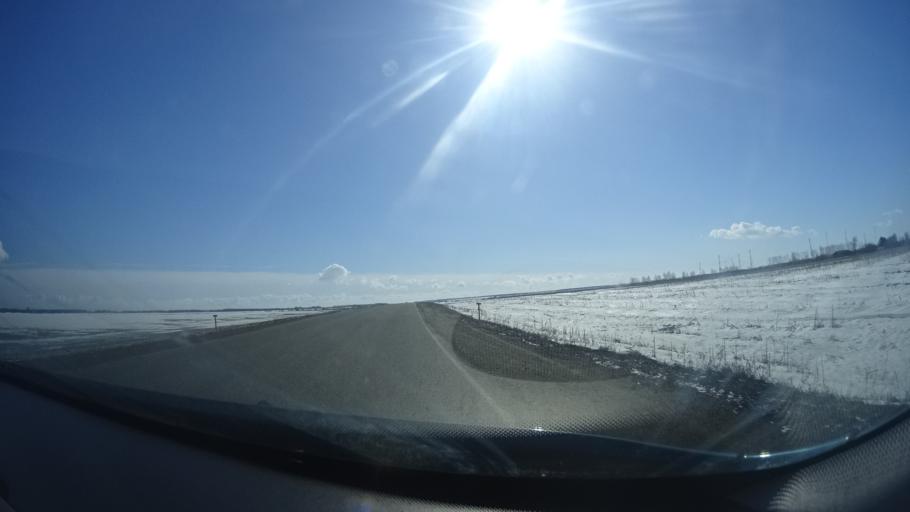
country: RU
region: Bashkortostan
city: Avdon
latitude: 54.6030
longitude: 55.8488
